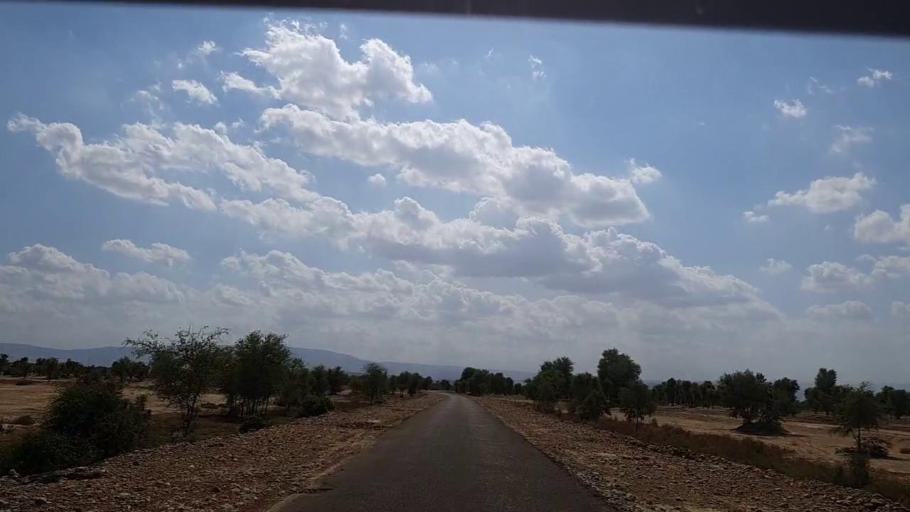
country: PK
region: Sindh
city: Johi
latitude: 26.5206
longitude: 67.4649
